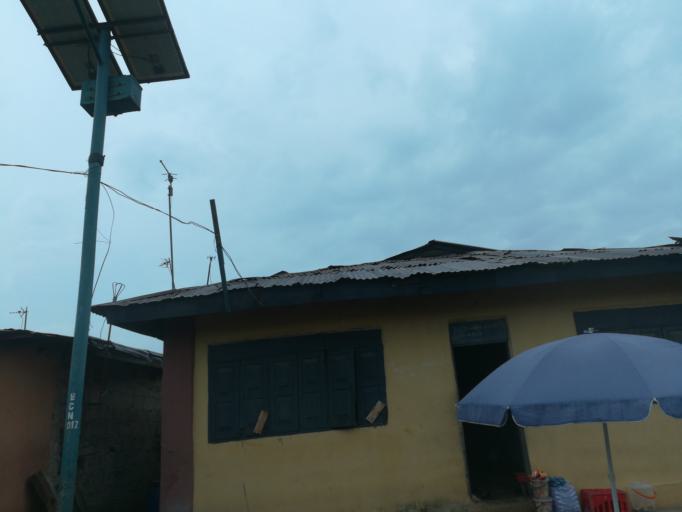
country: NG
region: Lagos
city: Oshodi
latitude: 6.5755
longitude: 3.3405
